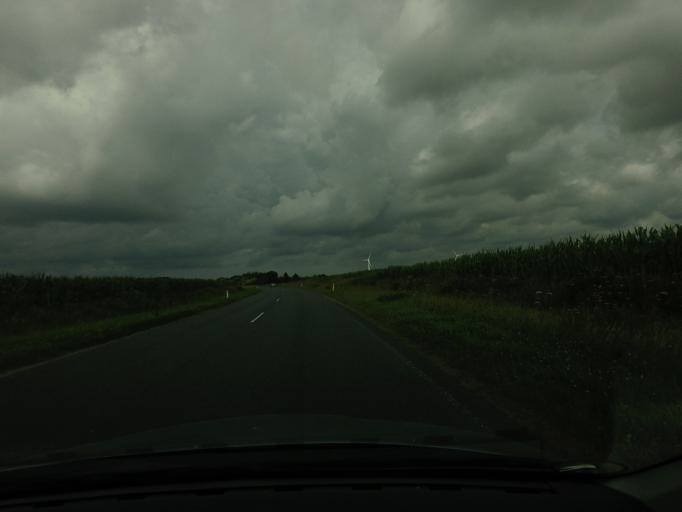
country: DK
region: North Denmark
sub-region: Hjorring Kommune
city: Tars
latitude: 57.4201
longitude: 10.0557
